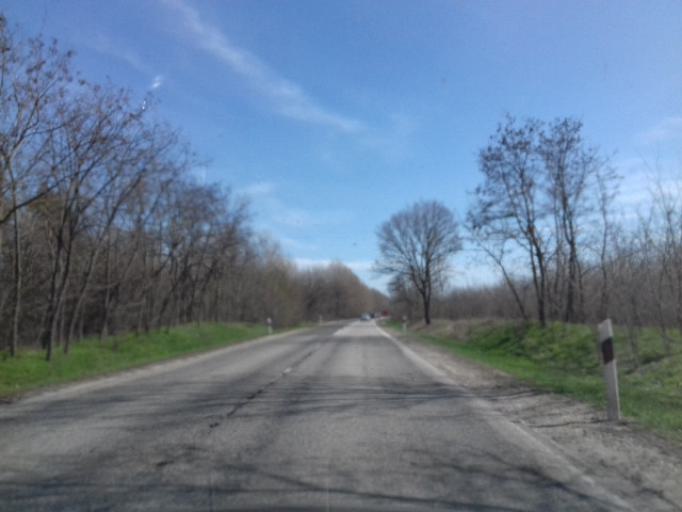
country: HU
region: Bacs-Kiskun
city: Nyarlorinc
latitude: 46.8902
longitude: 19.8330
